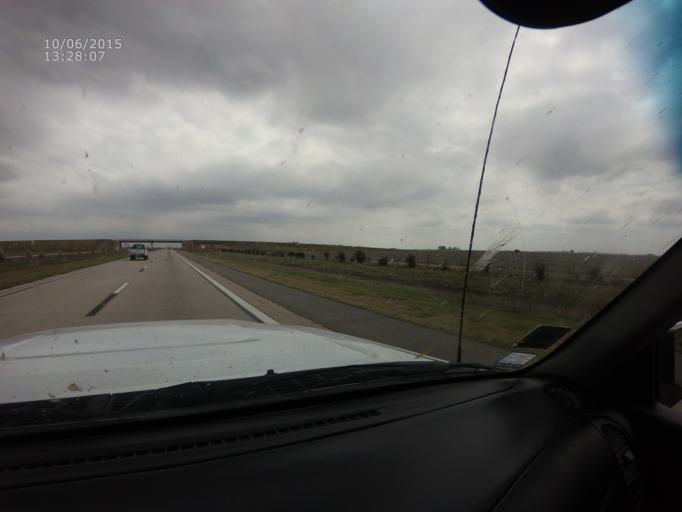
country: AR
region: Cordoba
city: Leones
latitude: -32.6433
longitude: -62.2168
